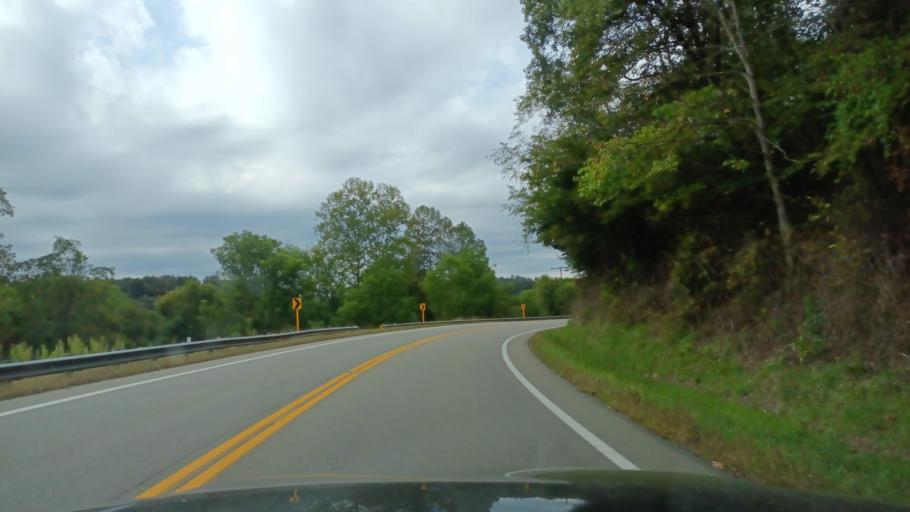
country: US
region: Ohio
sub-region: Vinton County
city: McArthur
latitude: 39.2698
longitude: -82.6534
